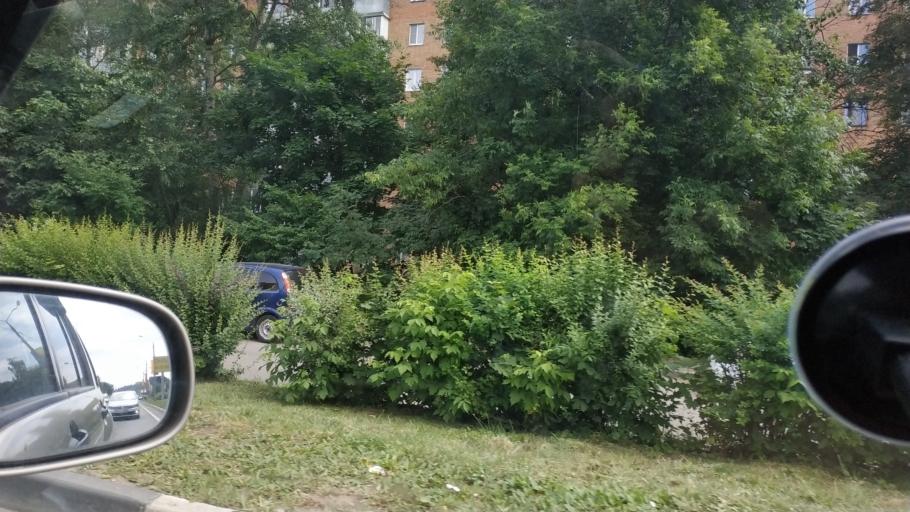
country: RU
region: Moskovskaya
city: Fryazino
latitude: 55.9504
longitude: 38.0495
